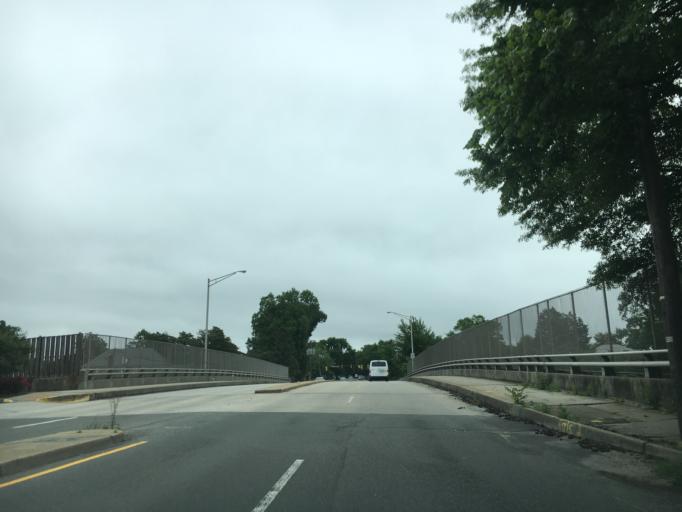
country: US
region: Virginia
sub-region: City of Richmond
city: Richmond
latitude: 37.5604
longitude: -77.4891
